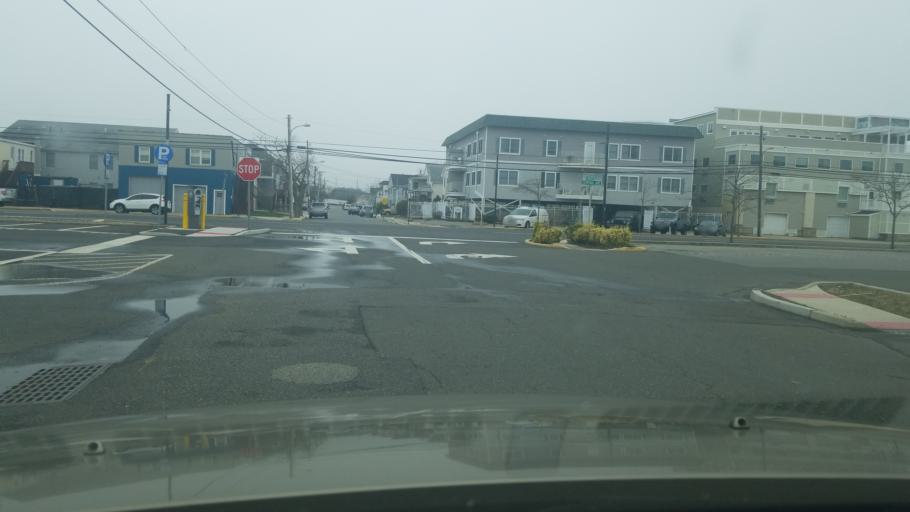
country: US
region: New Jersey
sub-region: Ocean County
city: Seaside Heights
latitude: 39.9407
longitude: -74.0750
